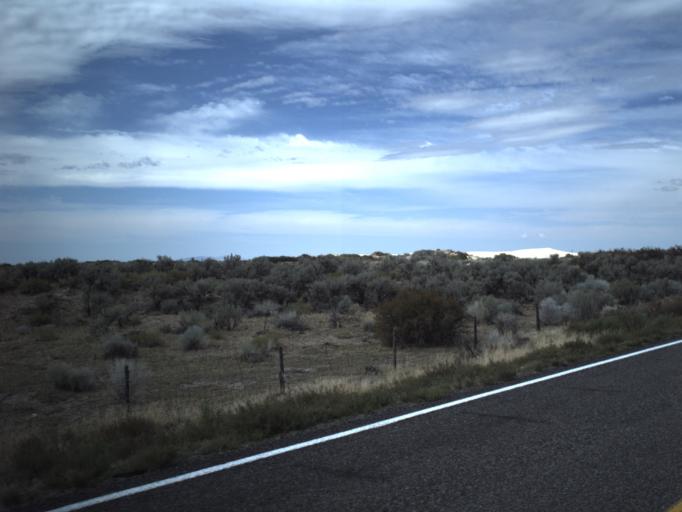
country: US
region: Utah
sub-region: Millard County
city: Fillmore
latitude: 39.1267
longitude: -112.4096
